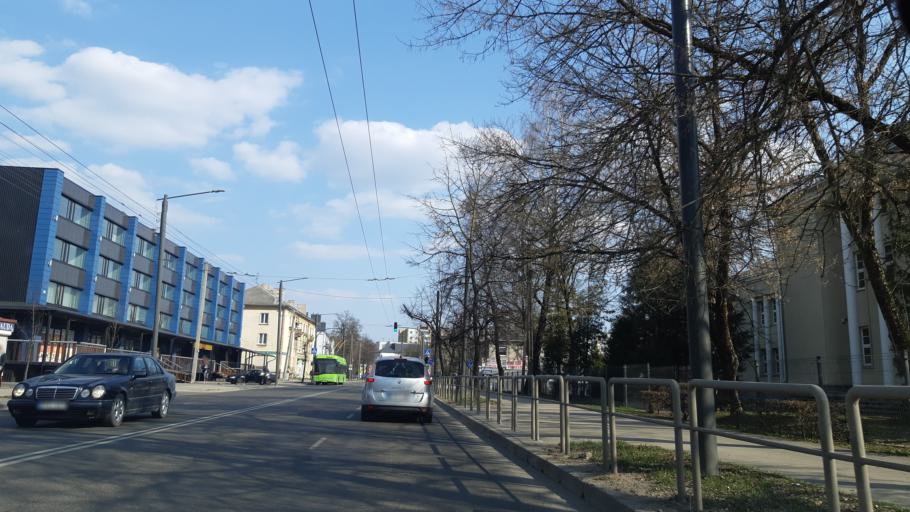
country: LT
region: Kauno apskritis
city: Dainava (Kaunas)
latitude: 54.8927
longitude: 23.9992
